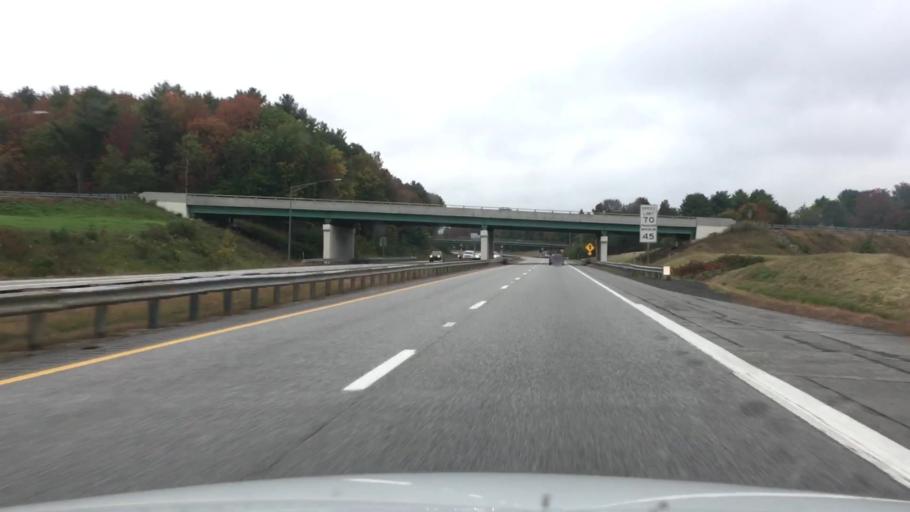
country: US
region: Maine
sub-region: Cumberland County
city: Falmouth
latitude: 43.7312
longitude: -70.3025
